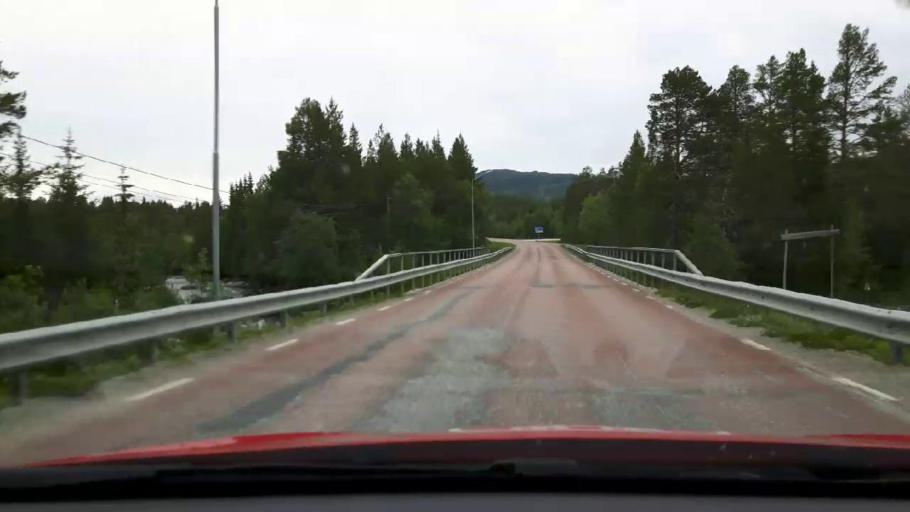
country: SE
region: Jaemtland
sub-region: Are Kommun
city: Are
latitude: 62.5545
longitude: 12.5674
